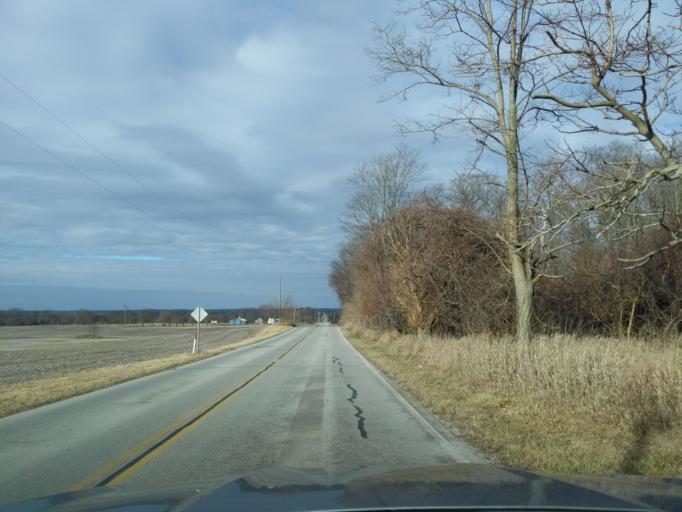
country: US
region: Indiana
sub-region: Tippecanoe County
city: Shadeland
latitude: 40.3395
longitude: -86.9756
